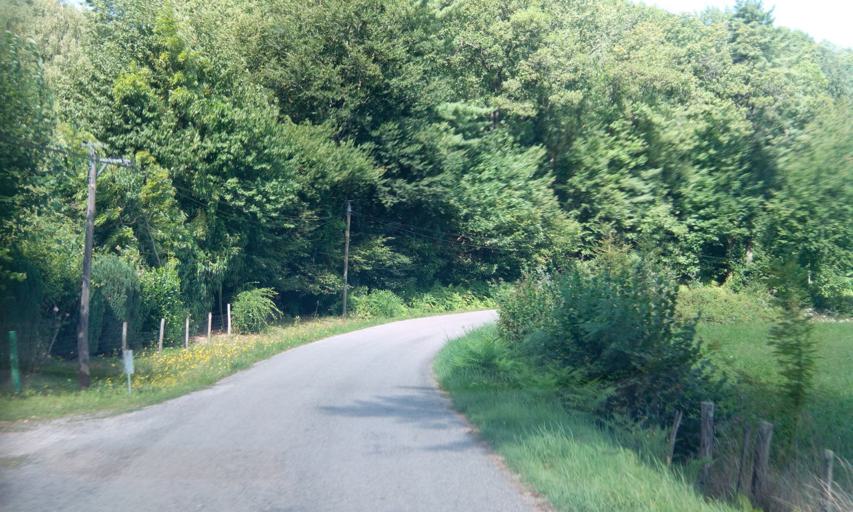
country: FR
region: Limousin
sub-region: Departement de la Haute-Vienne
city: Saint-Leonard-de-Noblat
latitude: 45.8206
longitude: 1.4733
